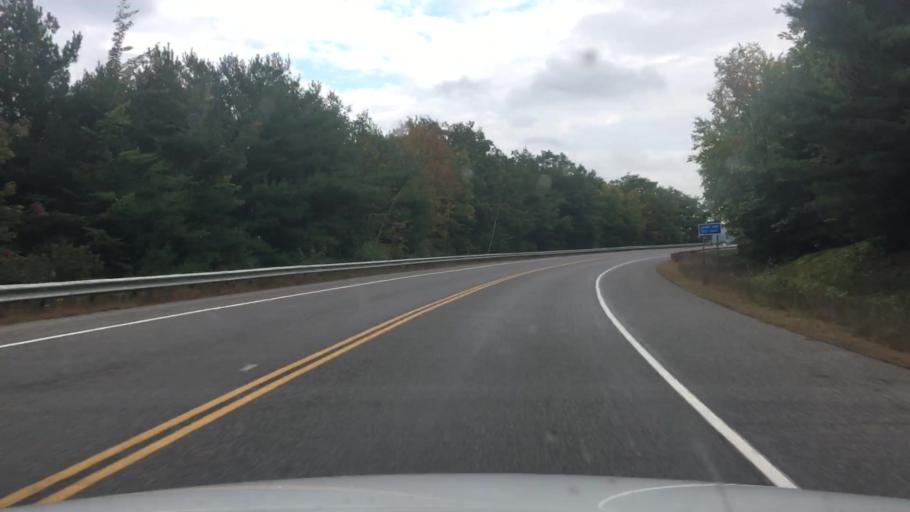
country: US
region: New Hampshire
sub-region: Carroll County
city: Wolfeboro
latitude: 43.5173
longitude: -71.2689
